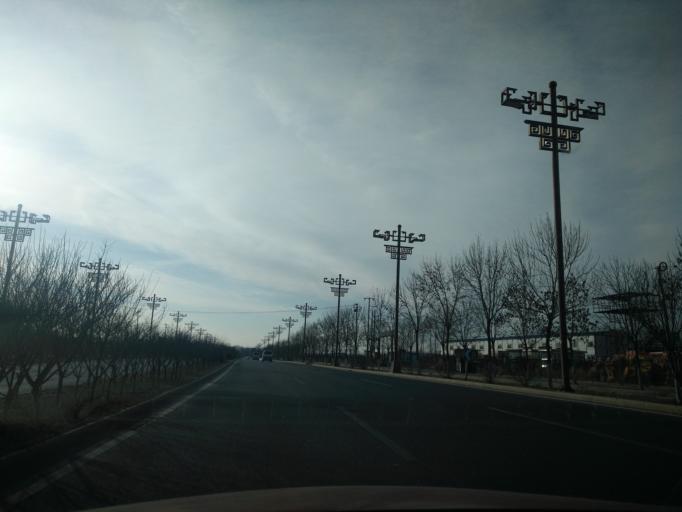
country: CN
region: Beijing
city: Jiugong
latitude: 39.7871
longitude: 116.4589
